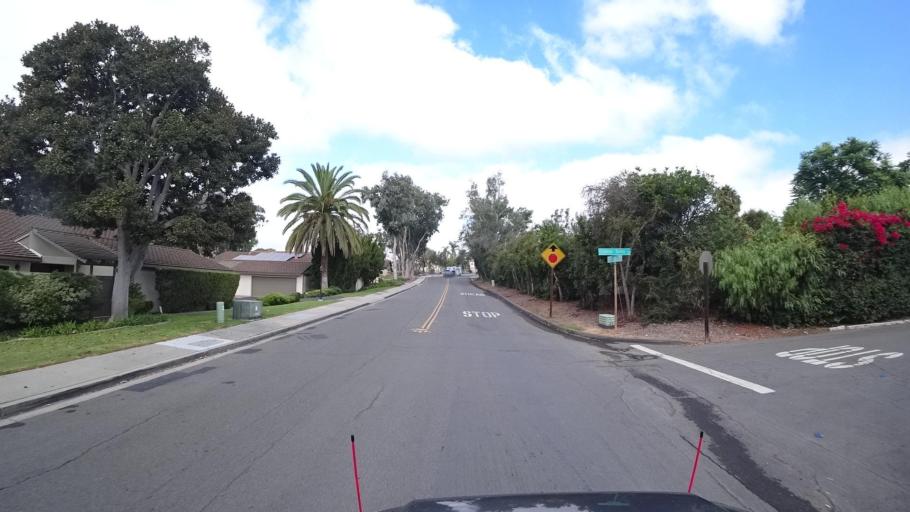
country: US
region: California
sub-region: San Diego County
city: Rancho Santa Fe
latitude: 33.0180
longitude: -117.2009
